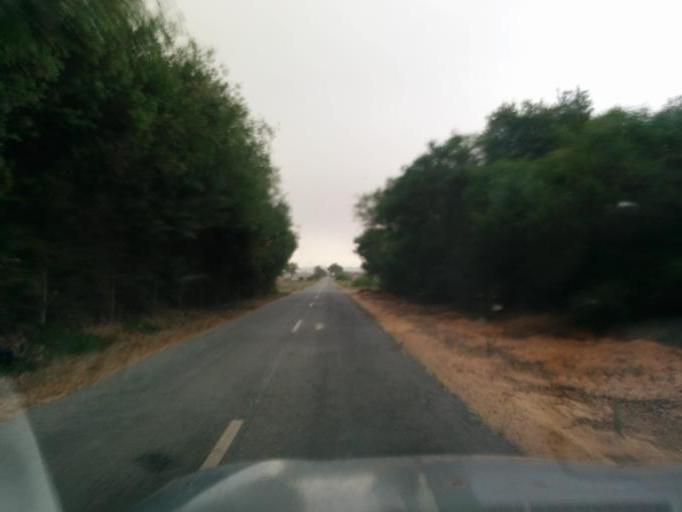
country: PT
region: Beja
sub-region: Odemira
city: Vila Nova de Milfontes
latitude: 37.6166
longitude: -8.7871
